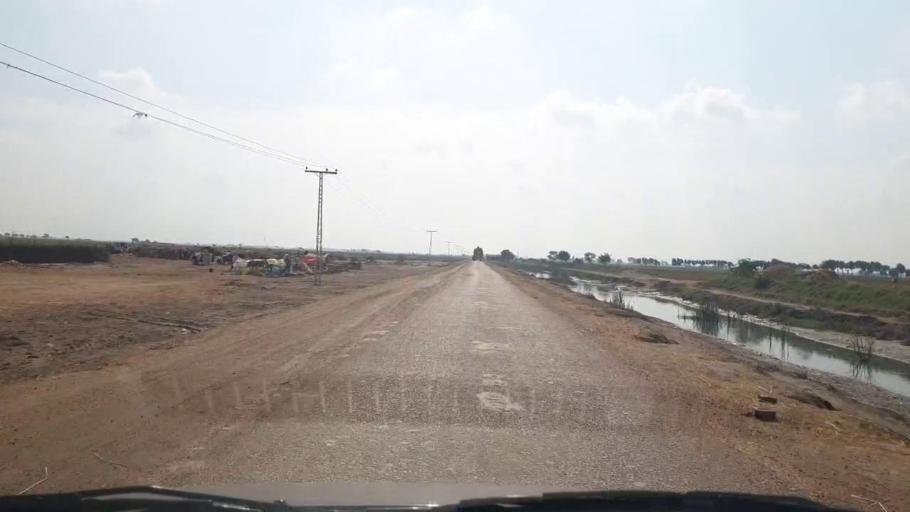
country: PK
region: Sindh
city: Kario
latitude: 24.6284
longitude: 68.5522
